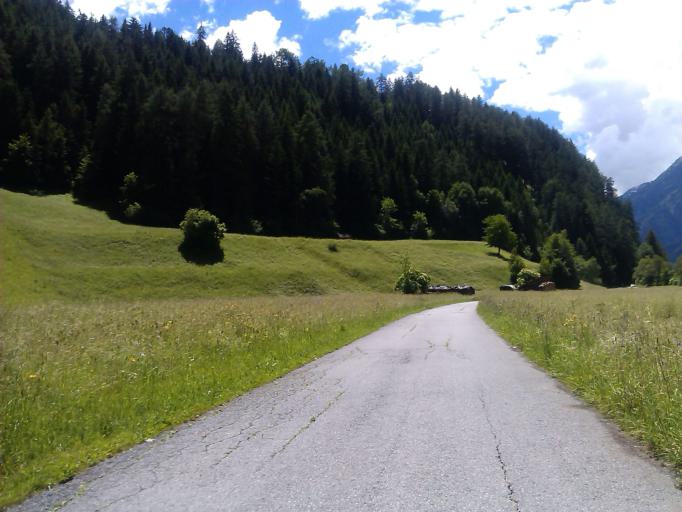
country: AT
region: Tyrol
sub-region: Politischer Bezirk Landeck
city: Pfunds
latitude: 46.9802
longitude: 10.5629
